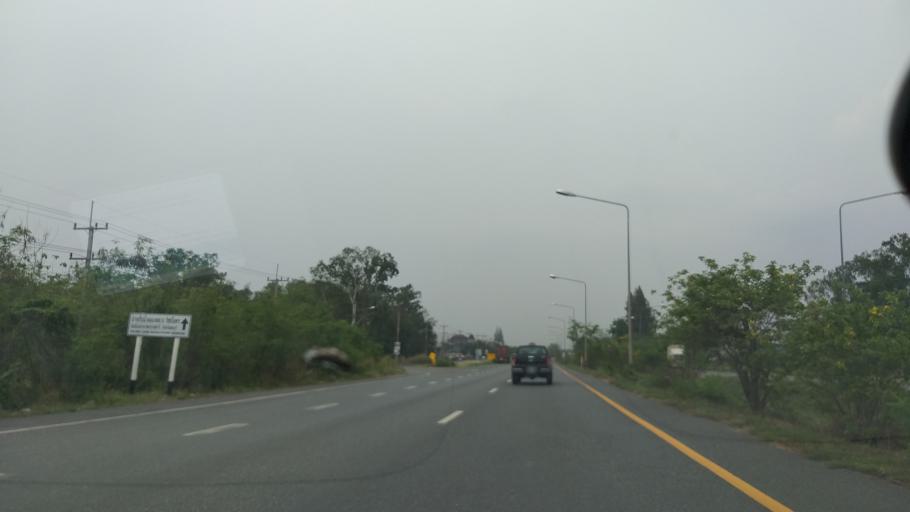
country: TH
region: Chon Buri
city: Ban Bueng
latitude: 13.2795
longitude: 101.2546
